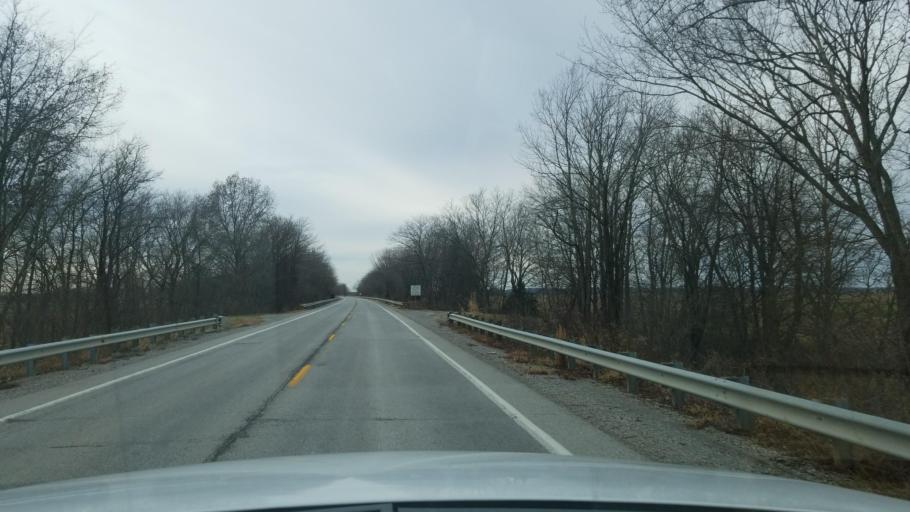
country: US
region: Indiana
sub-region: Posey County
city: Mount Vernon
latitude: 37.9398
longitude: -88.0691
